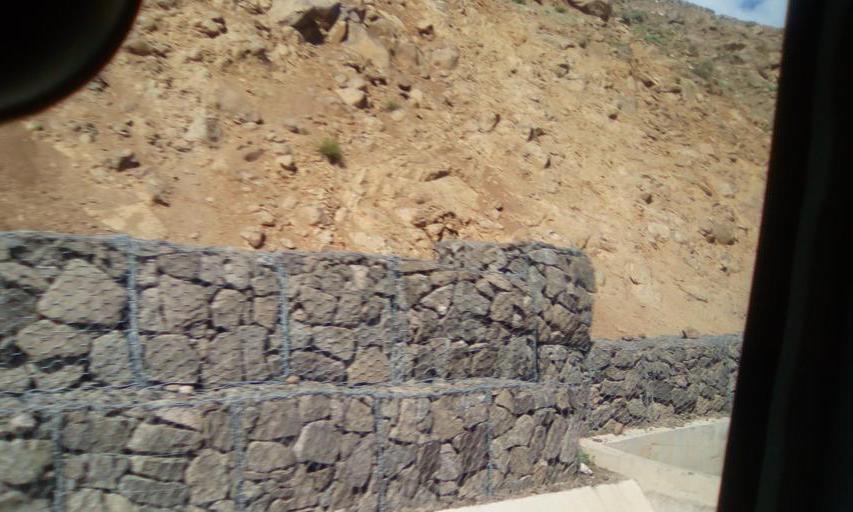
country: LS
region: Qacha's Nek
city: Qacha's Nek
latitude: -30.0043
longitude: 28.1587
